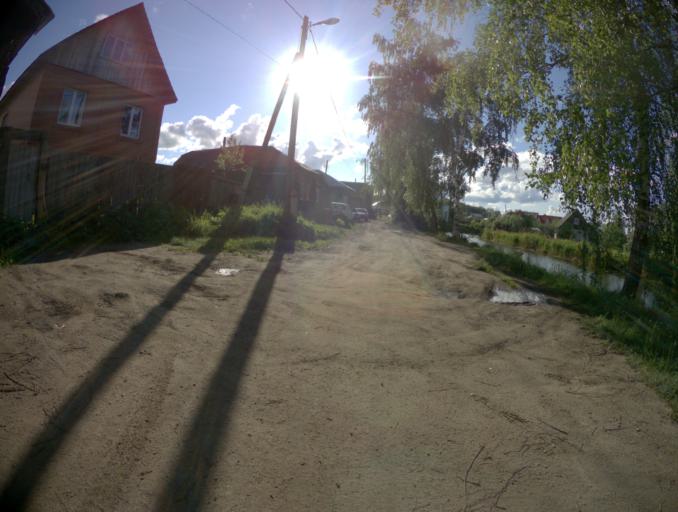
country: RU
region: Vladimir
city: Yur'yev-Pol'skiy
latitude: 56.4961
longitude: 39.6757
